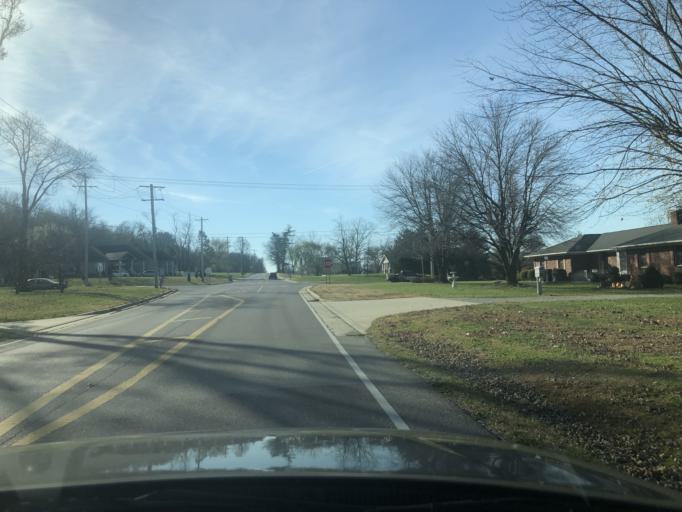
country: US
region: Indiana
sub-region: Warrick County
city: Newburgh
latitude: 37.9919
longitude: -87.4137
